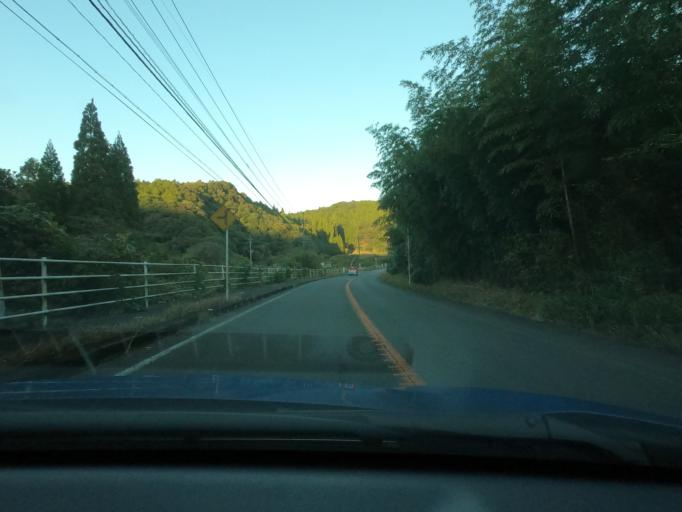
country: JP
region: Kagoshima
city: Satsumasendai
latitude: 31.8129
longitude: 130.3719
